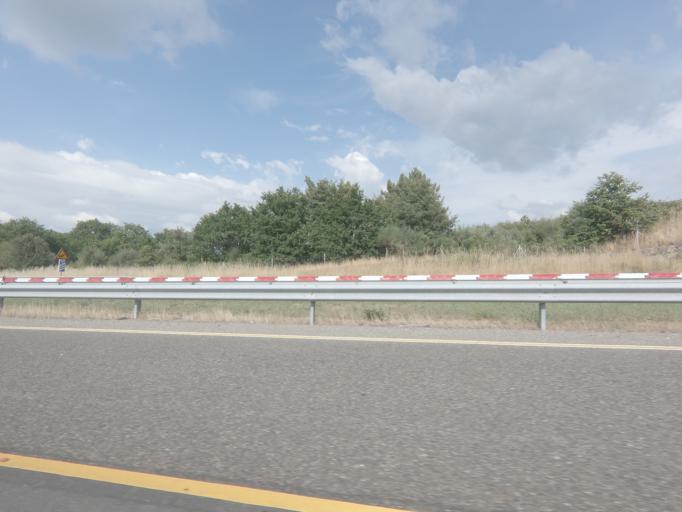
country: ES
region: Galicia
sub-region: Provincia de Ourense
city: Taboadela
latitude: 42.2430
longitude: -7.8598
